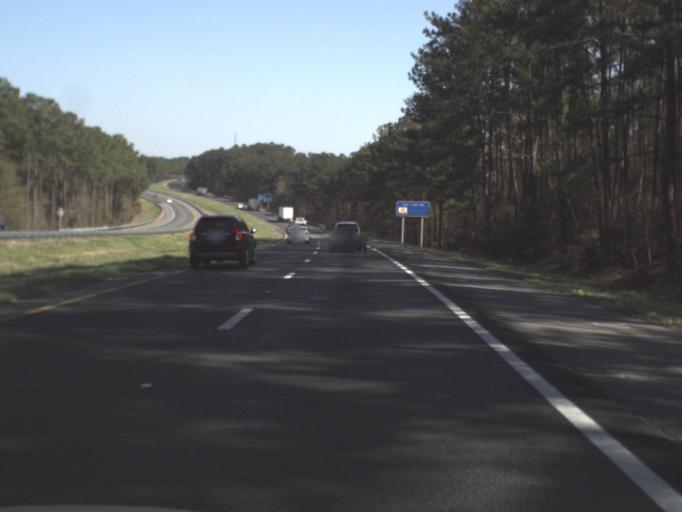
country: US
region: Florida
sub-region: Gadsden County
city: Chattahoochee
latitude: 30.6189
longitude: -84.8335
